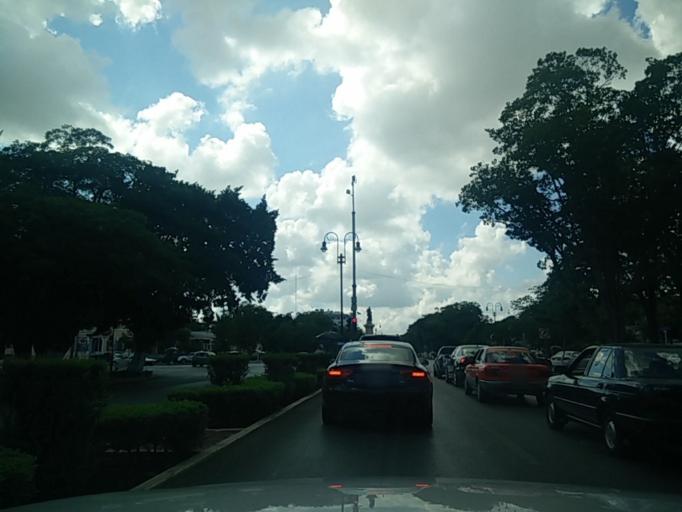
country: MX
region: Yucatan
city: Merida
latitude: 20.9867
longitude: -89.6175
